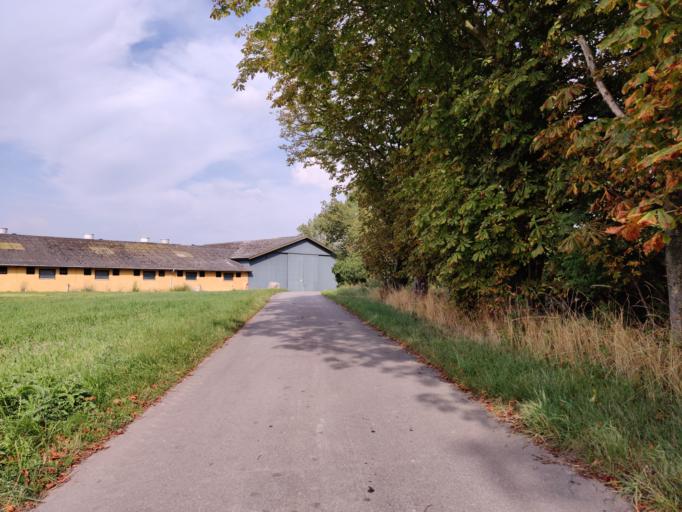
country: DK
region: Zealand
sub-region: Guldborgsund Kommune
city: Nykobing Falster
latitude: 54.6997
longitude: 11.9062
